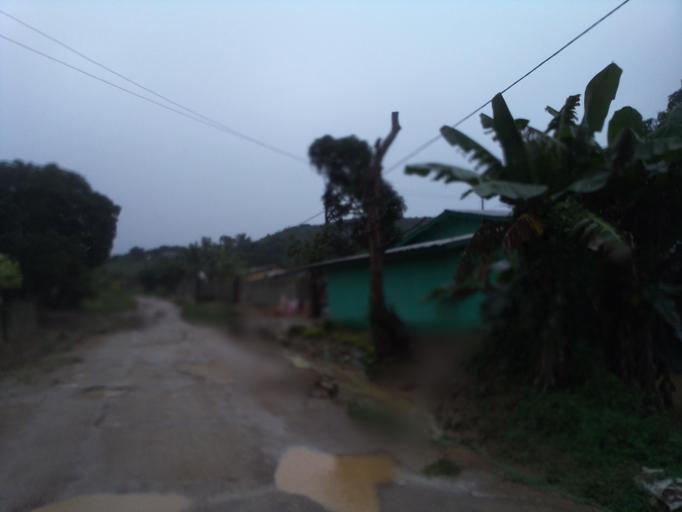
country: SL
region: Eastern Province
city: Kenema
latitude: 7.8563
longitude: -11.1919
